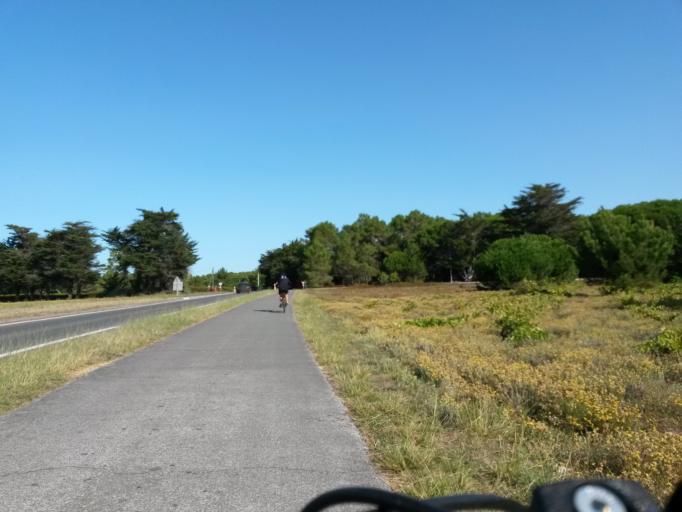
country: FR
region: Poitou-Charentes
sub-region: Departement de la Charente-Maritime
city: Saint-Martin-de-Re
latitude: 46.1693
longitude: -1.3622
